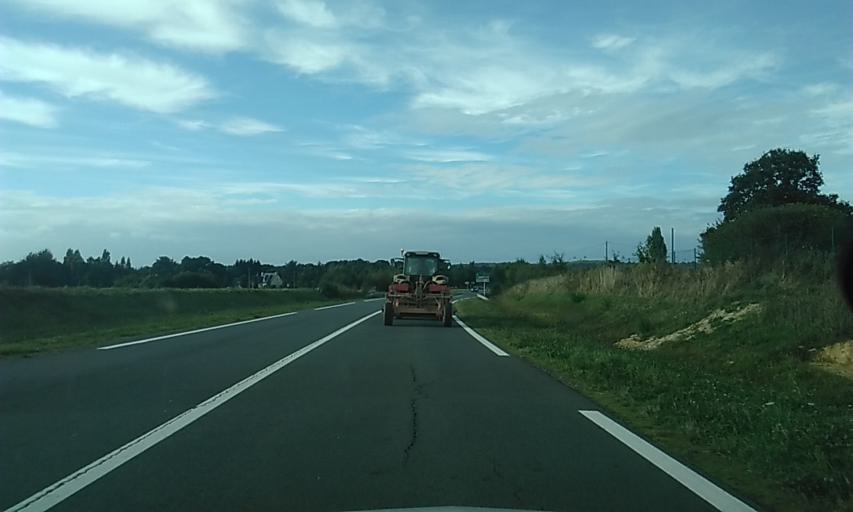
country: FR
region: Brittany
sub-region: Departement d'Ille-et-Vilaine
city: Bedee
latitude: 48.1858
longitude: -1.9396
